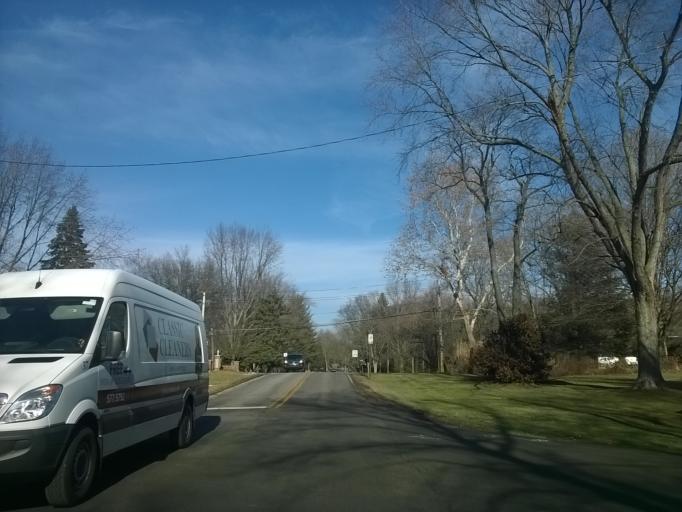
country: US
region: Indiana
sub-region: Marion County
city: Broad Ripple
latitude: 39.8905
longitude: -86.0983
